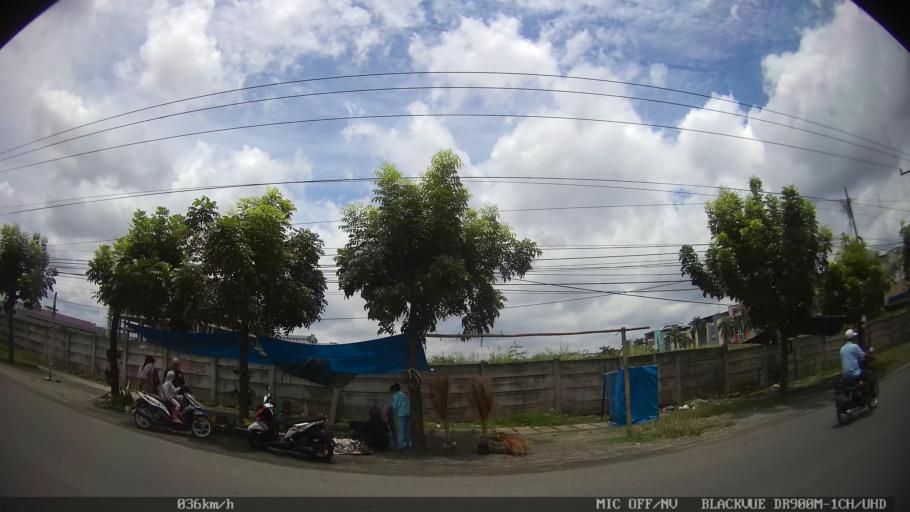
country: ID
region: North Sumatra
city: Medan
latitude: 3.6011
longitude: 98.7119
